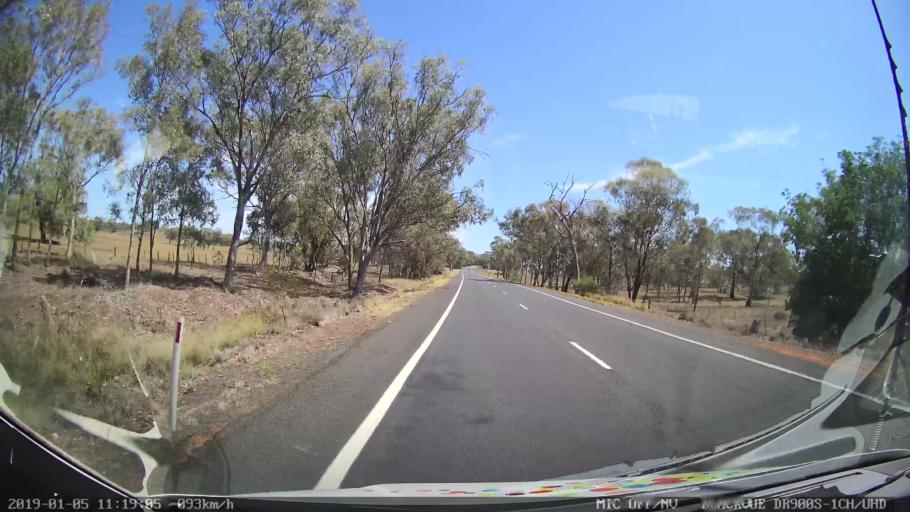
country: AU
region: New South Wales
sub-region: Warrumbungle Shire
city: Coonabarabran
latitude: -31.3083
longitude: 149.2975
